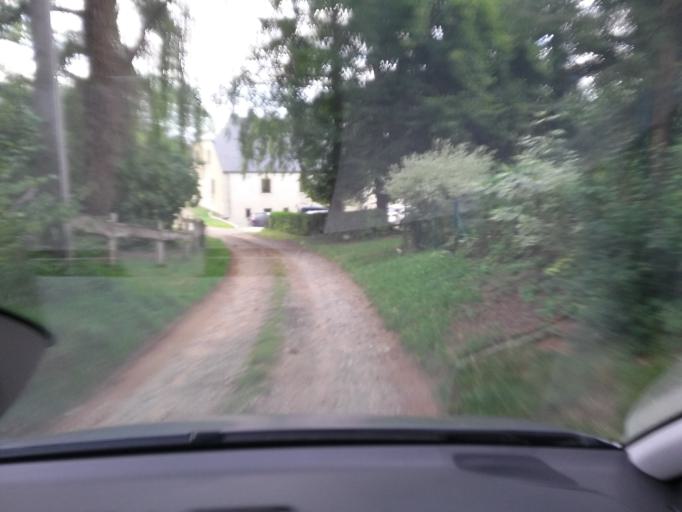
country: BE
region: Wallonia
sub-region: Province du Luxembourg
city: Arlon
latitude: 49.6912
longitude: 5.7984
